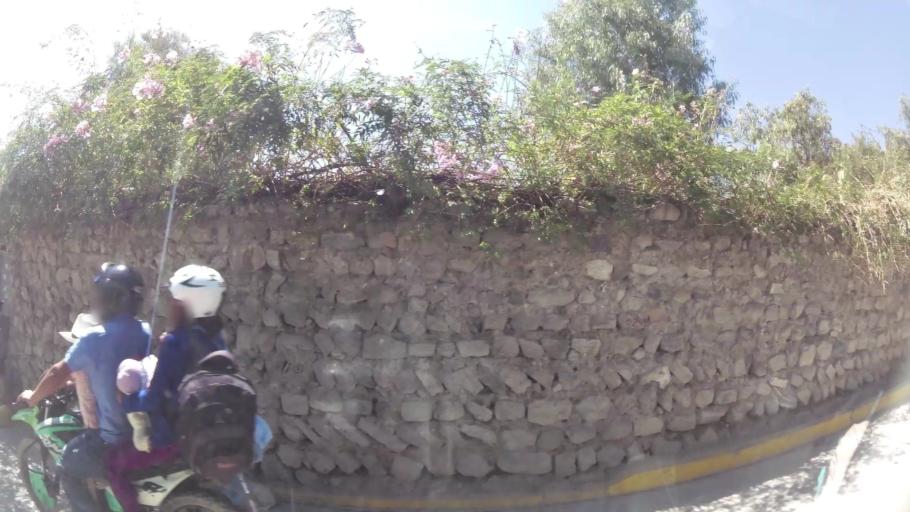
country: PE
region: Ayacucho
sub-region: Provincia de Huamanga
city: Carmen Alto
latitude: -13.1770
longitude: -74.2265
